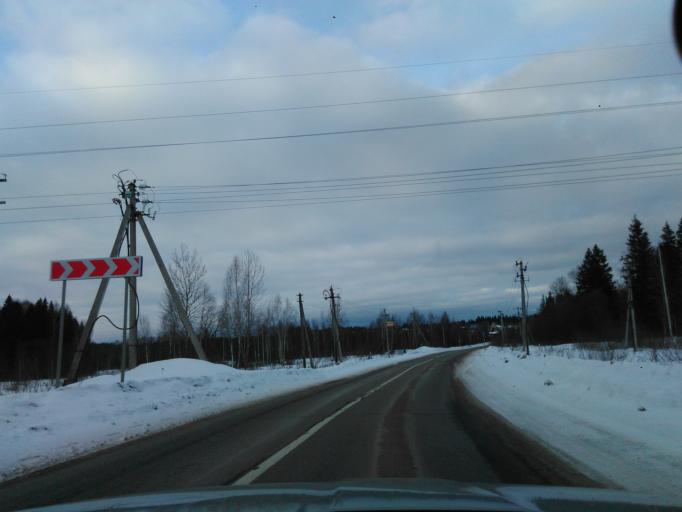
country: RU
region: Moskovskaya
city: Dedenevo
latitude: 56.2869
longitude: 37.5658
